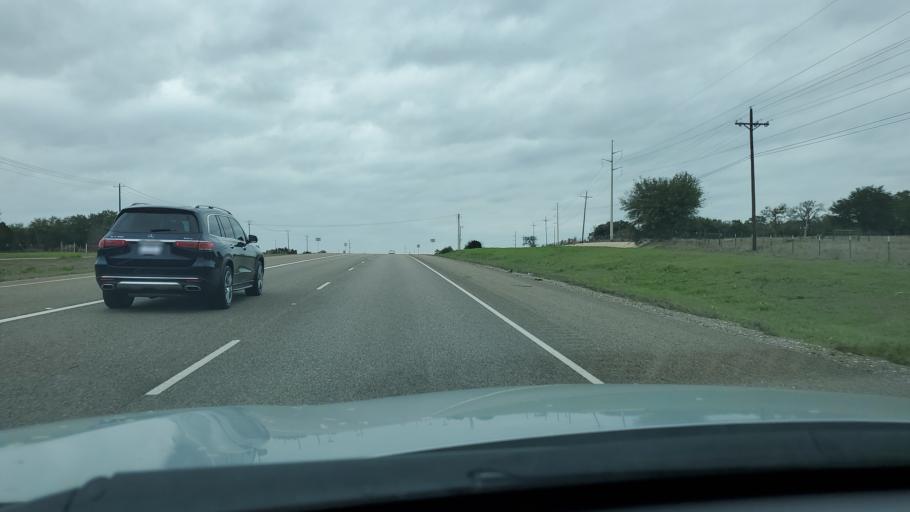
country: US
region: Texas
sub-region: Williamson County
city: Serenada
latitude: 30.7608
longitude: -97.7389
